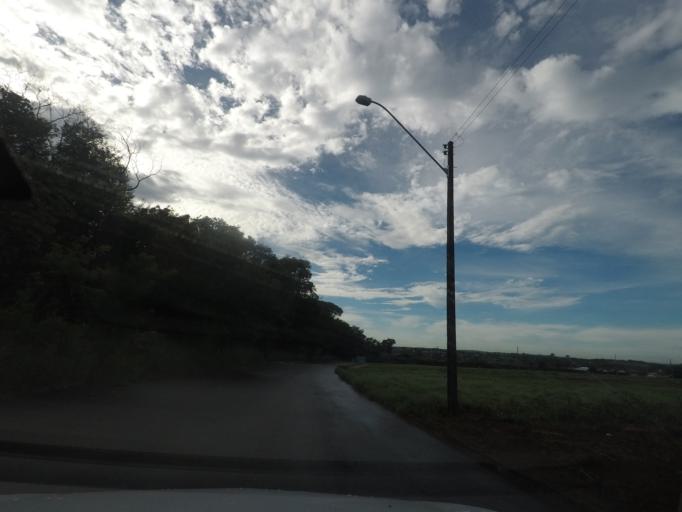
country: BR
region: Goias
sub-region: Aparecida De Goiania
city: Aparecida de Goiania
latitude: -16.7807
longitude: -49.3821
